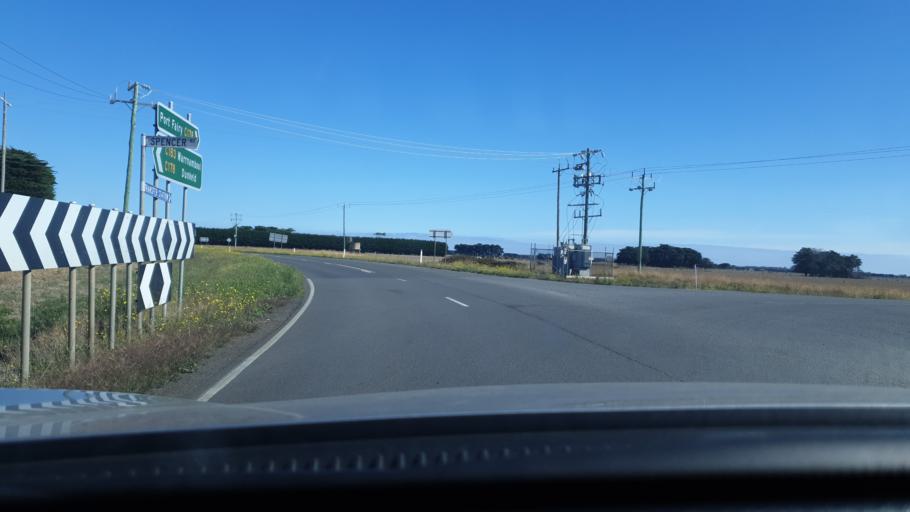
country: AU
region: Victoria
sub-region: Moyne
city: Port Fairy
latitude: -38.2855
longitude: 142.3107
